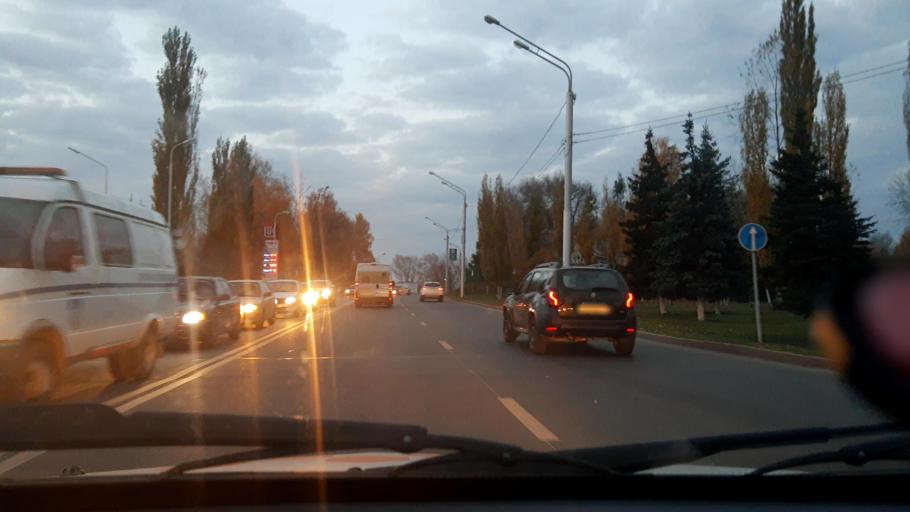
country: RU
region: Bashkortostan
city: Mikhaylovka
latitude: 54.7045
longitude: 55.8468
